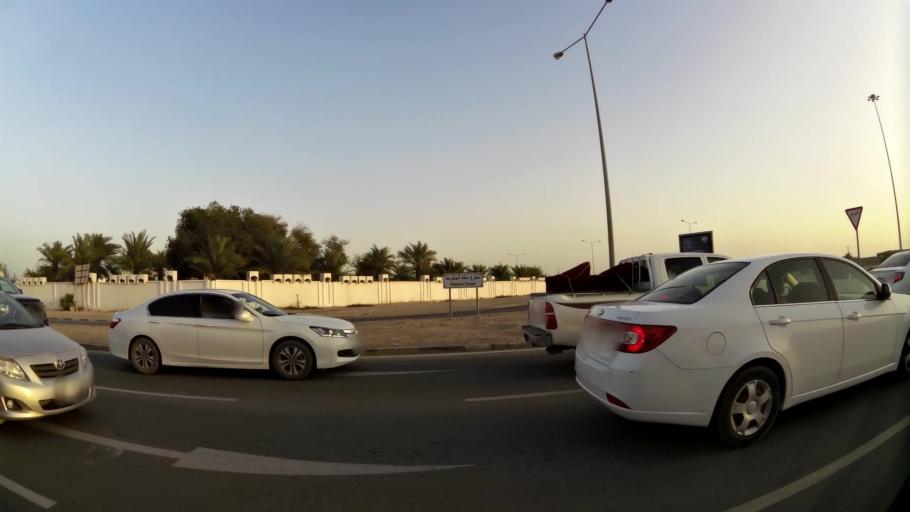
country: QA
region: Baladiyat ar Rayyan
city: Ar Rayyan
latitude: 25.3129
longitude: 51.4610
